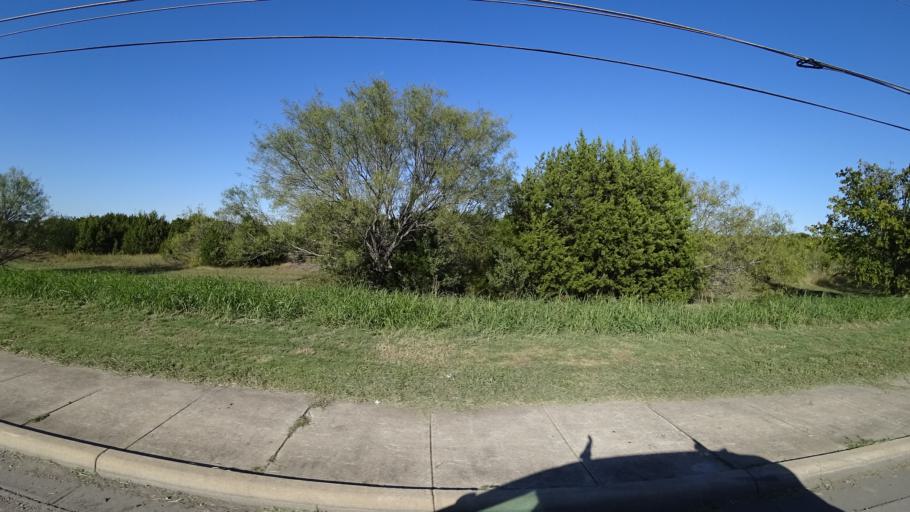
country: US
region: Texas
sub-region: Travis County
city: Hornsby Bend
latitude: 30.2944
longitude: -97.6343
